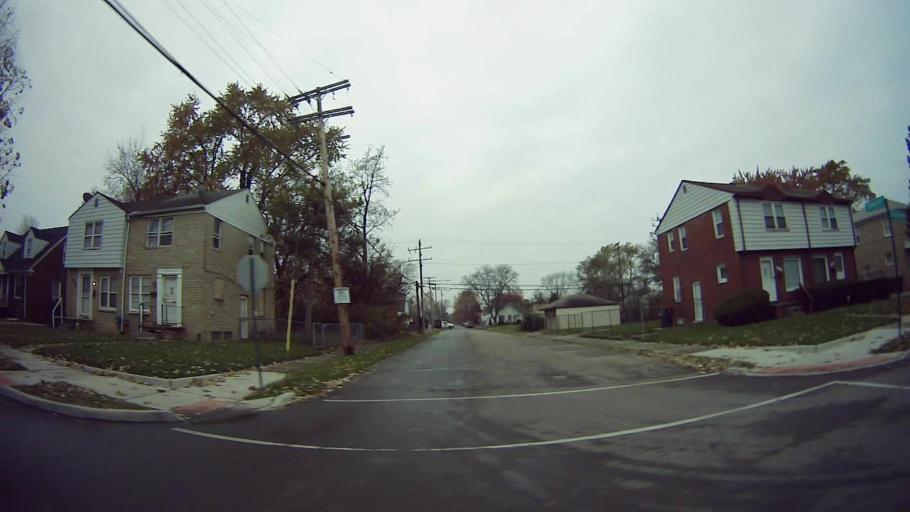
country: US
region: Michigan
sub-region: Wayne County
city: Dearborn Heights
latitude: 42.3468
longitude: -83.2355
